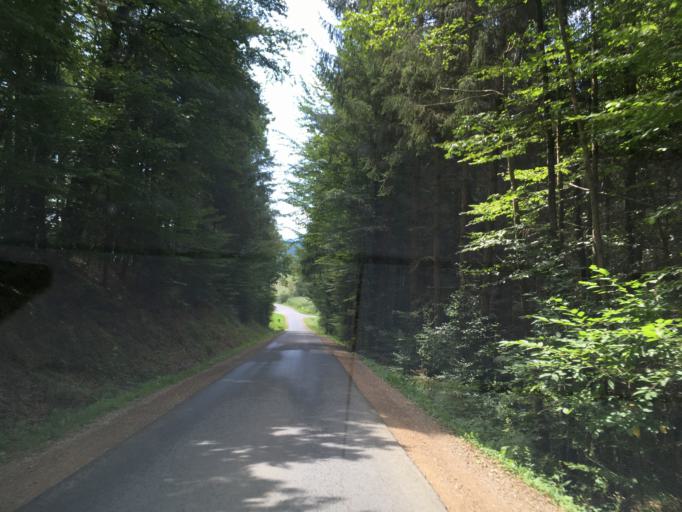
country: AT
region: Styria
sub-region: Politischer Bezirk Leibnitz
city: Pistorf
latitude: 46.7686
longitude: 15.3926
